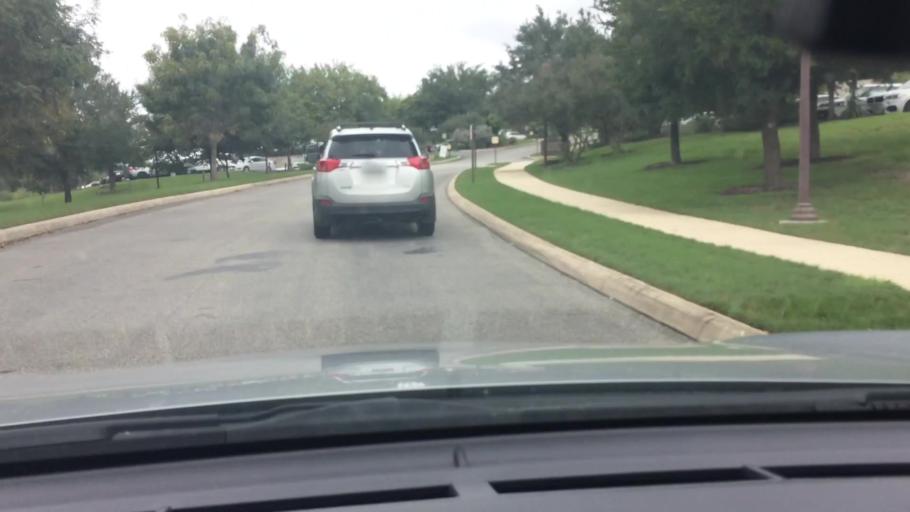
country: US
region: Texas
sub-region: Bexar County
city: Timberwood Park
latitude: 29.6641
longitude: -98.4006
